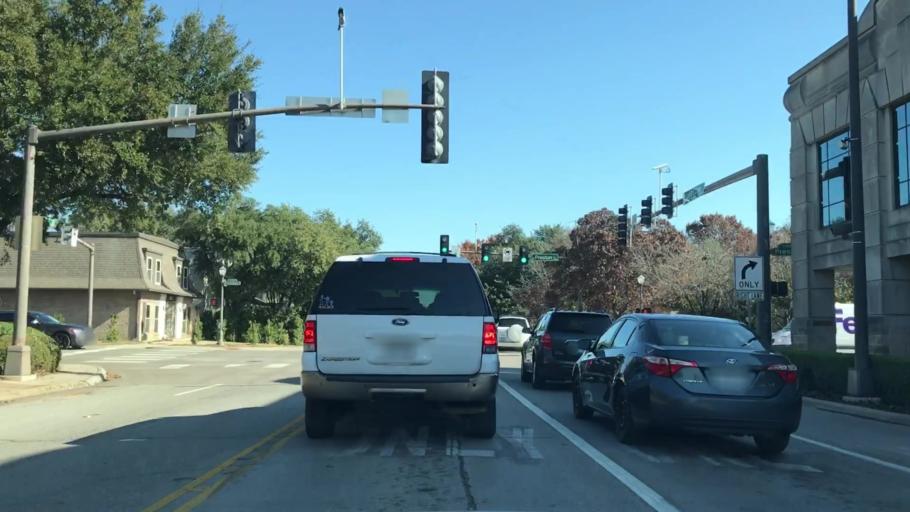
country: US
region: Texas
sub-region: Dallas County
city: University Park
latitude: 32.8511
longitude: -96.8047
